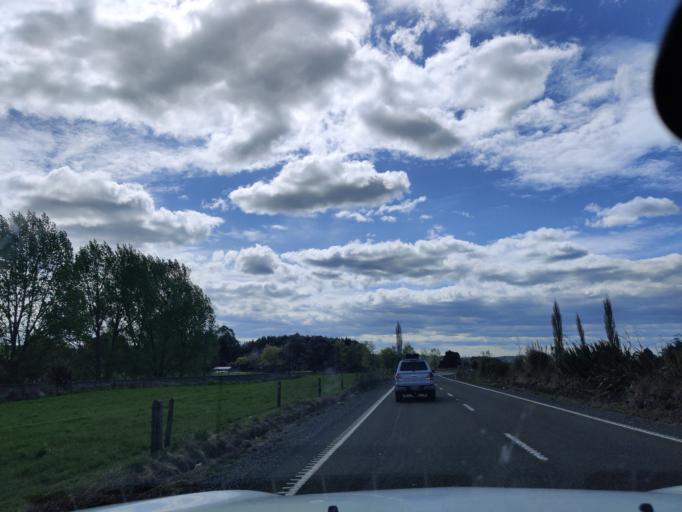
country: NZ
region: Waikato
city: Turangi
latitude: -39.0241
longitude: 175.3808
